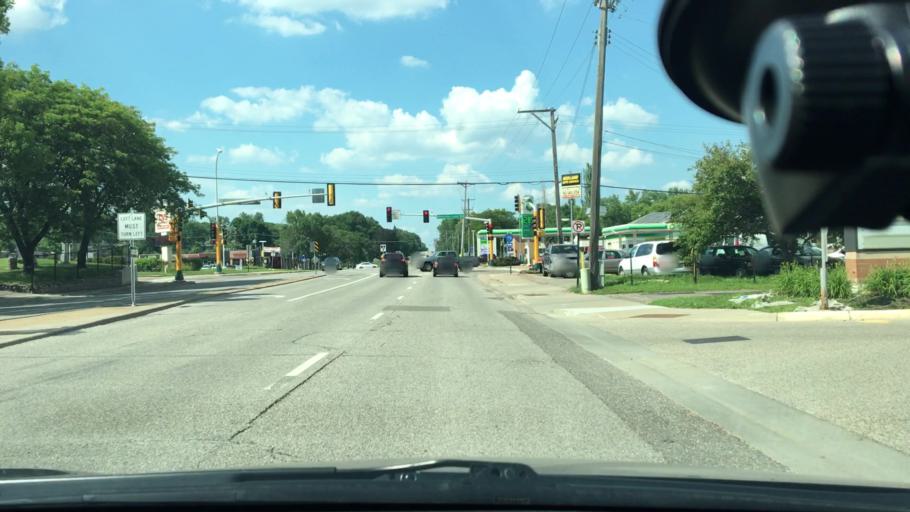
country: US
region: Minnesota
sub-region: Hennepin County
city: Golden Valley
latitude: 45.0066
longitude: -93.3802
